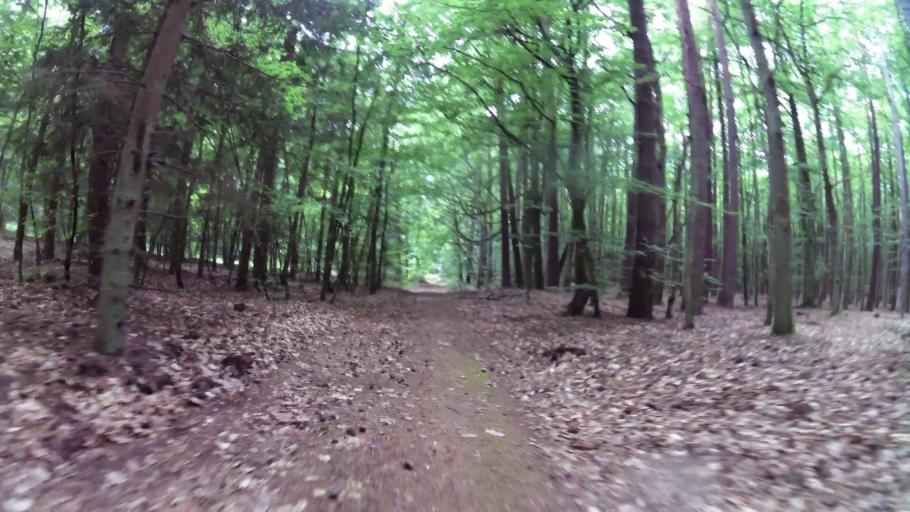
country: PL
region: West Pomeranian Voivodeship
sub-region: Powiat kamienski
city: Miedzyzdroje
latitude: 53.9327
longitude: 14.5320
